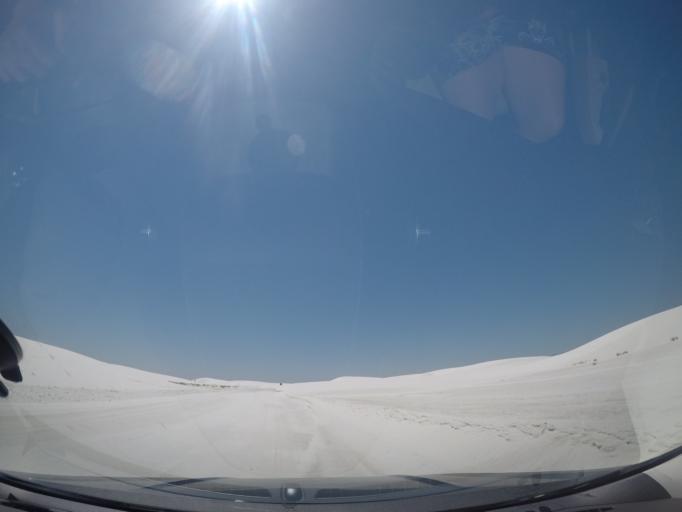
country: US
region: New Mexico
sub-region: Otero County
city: Holloman Air Force Base
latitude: 32.8176
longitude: -106.2703
